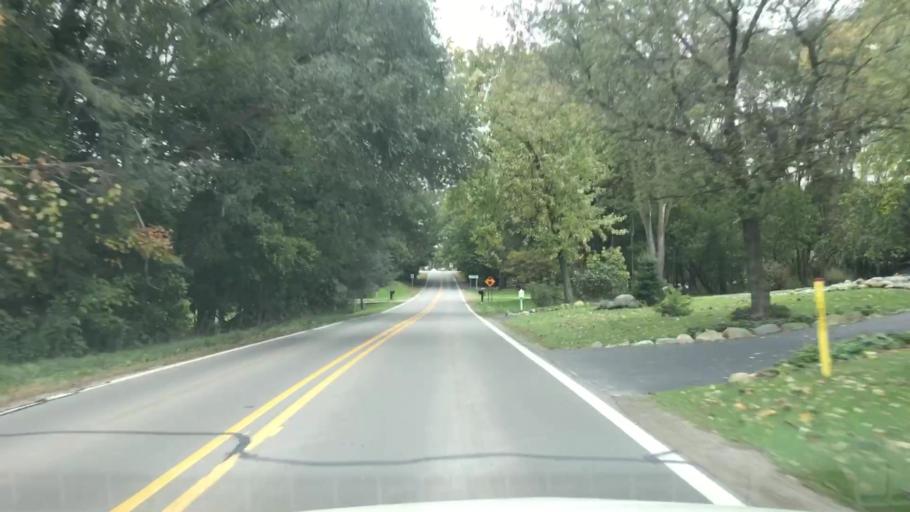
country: US
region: Michigan
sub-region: Macomb County
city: Shelby
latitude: 42.7422
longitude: -83.0603
